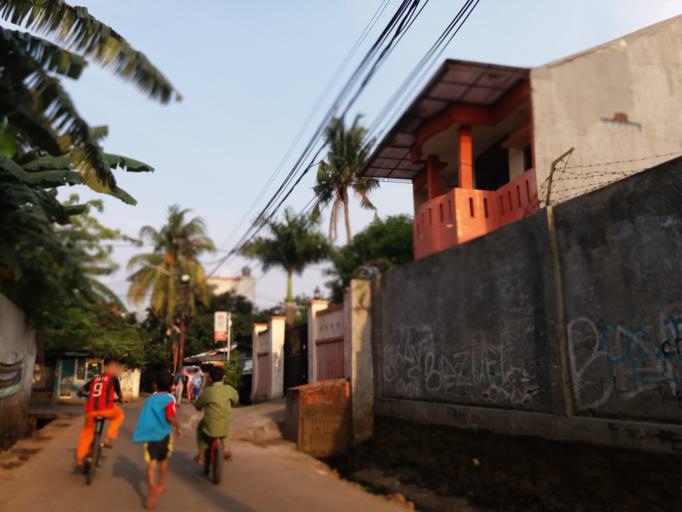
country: ID
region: Jakarta Raya
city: Jakarta
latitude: -6.2441
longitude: 106.8136
